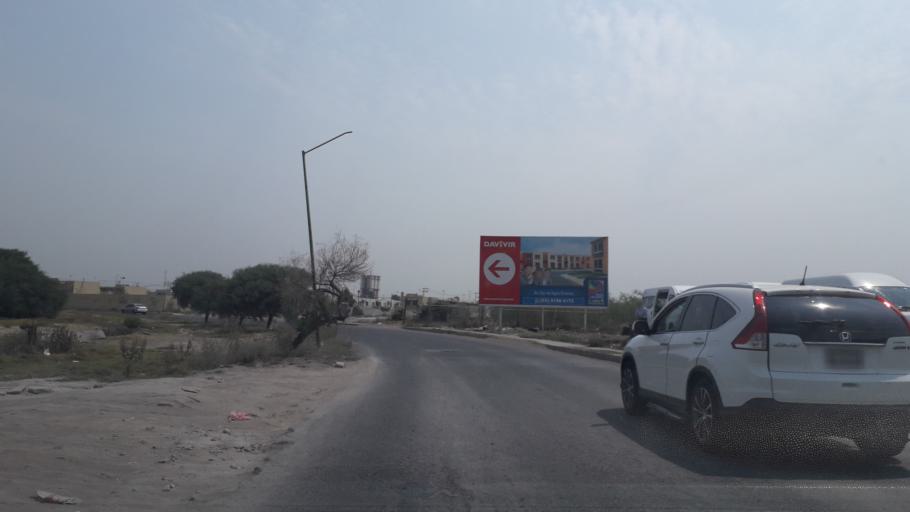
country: MX
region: Mexico
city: Santo Tomas Chiconautla
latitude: 19.6407
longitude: -99.0233
